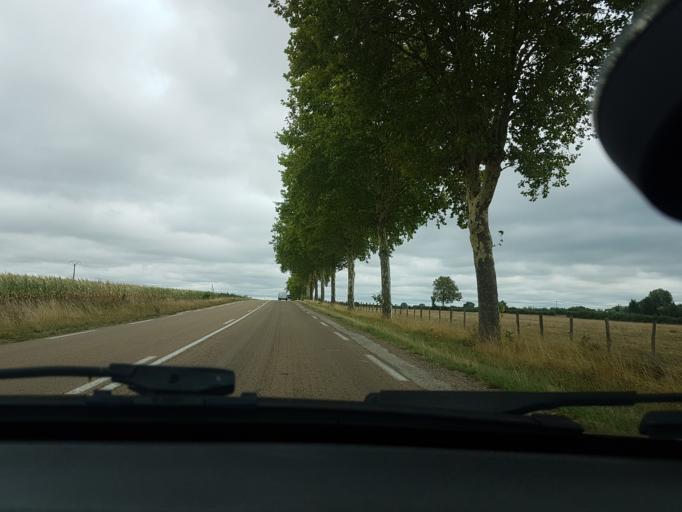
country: FR
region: Bourgogne
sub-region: Departement de l'Yonne
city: Avallon
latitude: 47.4900
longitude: 3.9807
